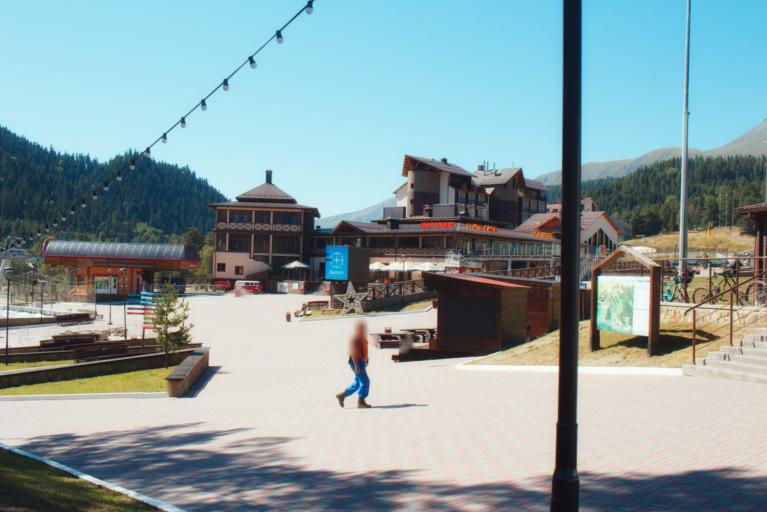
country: RU
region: Karachayevo-Cherkesiya
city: Nizhniy Arkhyz
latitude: 43.5439
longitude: 41.1818
